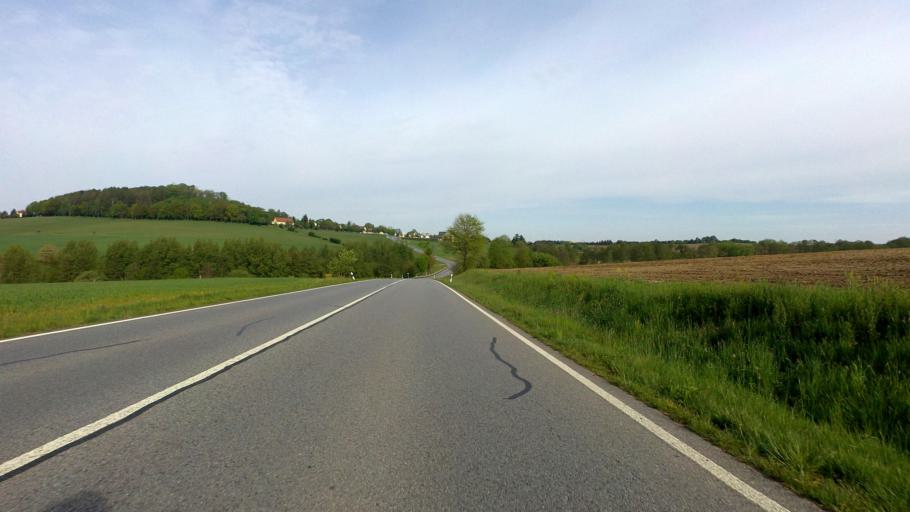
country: DE
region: Saxony
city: Stolpen
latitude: 51.0468
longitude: 14.0961
